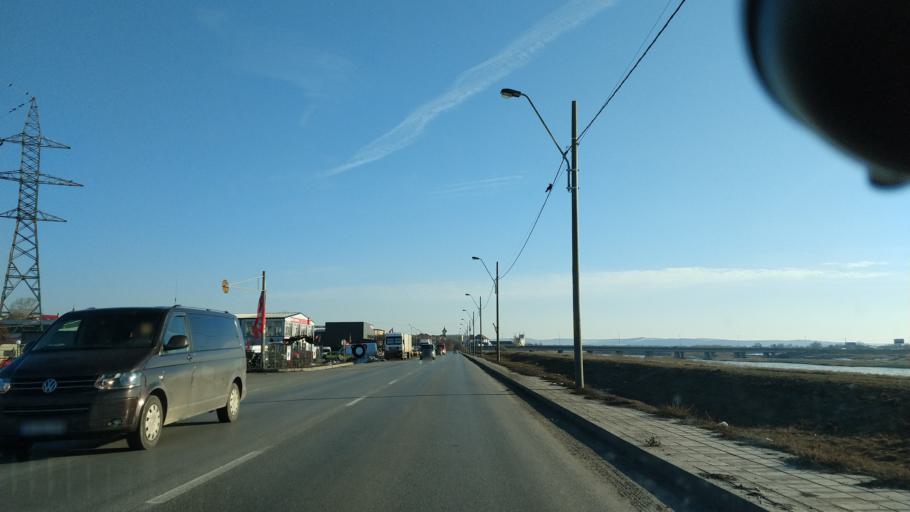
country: RO
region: Neamt
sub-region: Municipiul Roman
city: Roman
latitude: 46.9201
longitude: 26.9168
